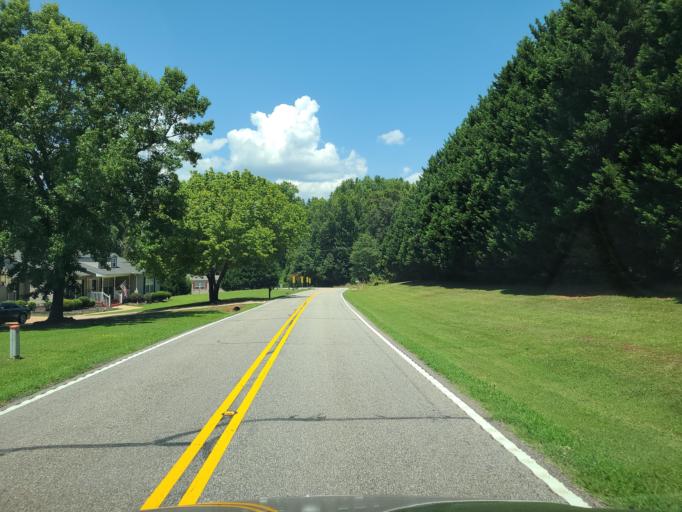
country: US
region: South Carolina
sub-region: Spartanburg County
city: Duncan
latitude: 34.9746
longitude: -82.1755
